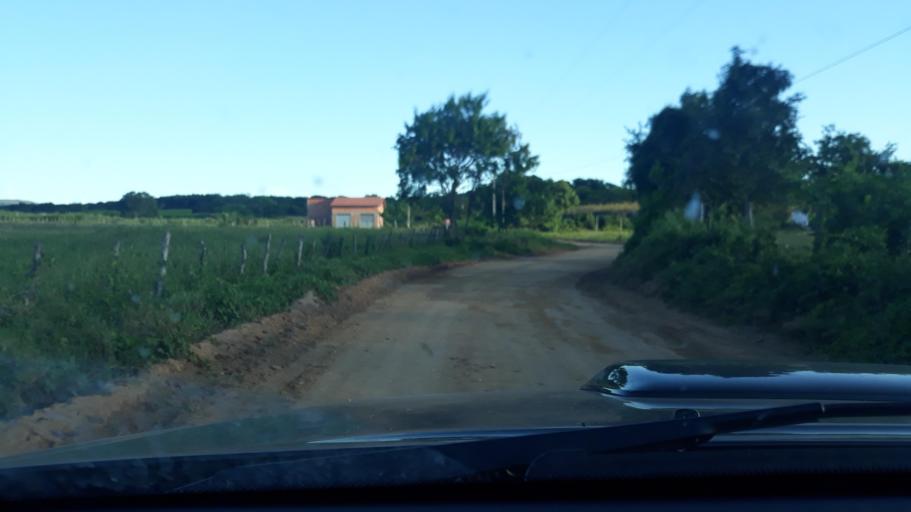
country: BR
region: Bahia
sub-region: Riacho De Santana
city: Riacho de Santana
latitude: -13.8328
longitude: -42.7294
